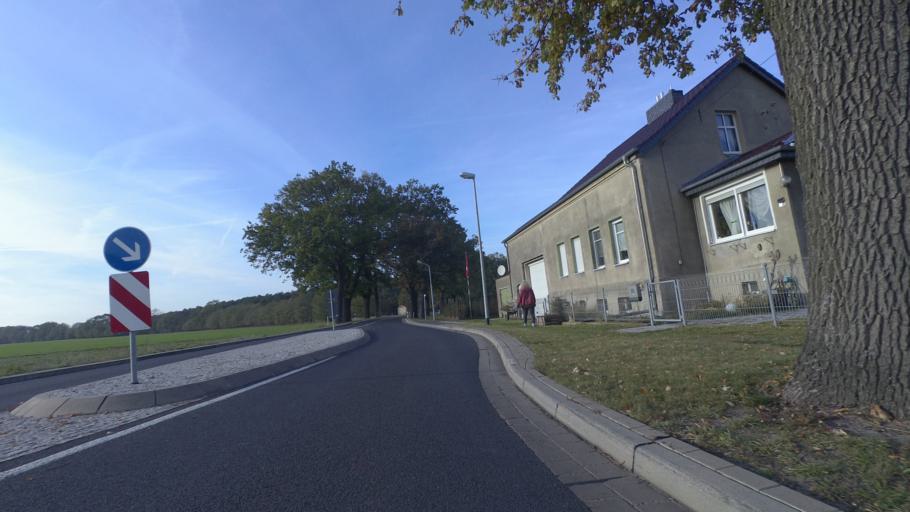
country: DE
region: Brandenburg
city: Sperenberg
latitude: 52.1909
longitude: 13.3210
